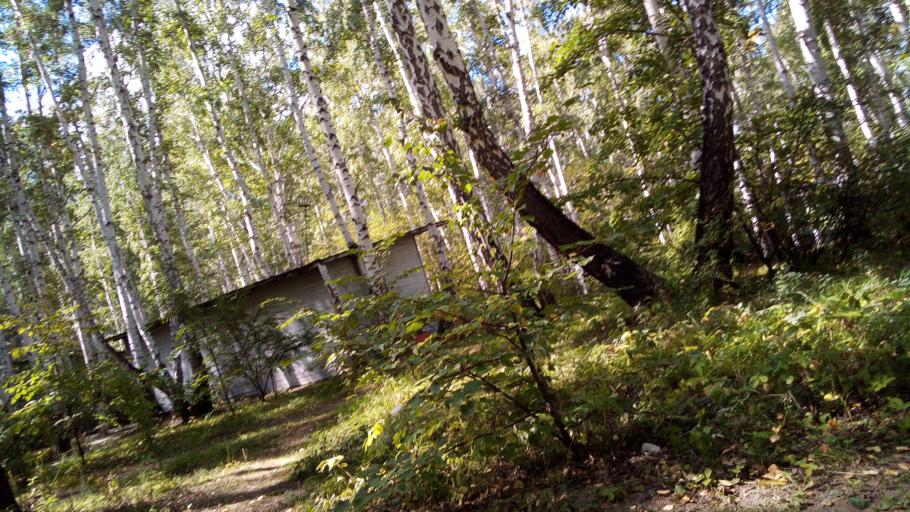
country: RU
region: Chelyabinsk
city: Tayginka
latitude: 55.4769
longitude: 60.4955
